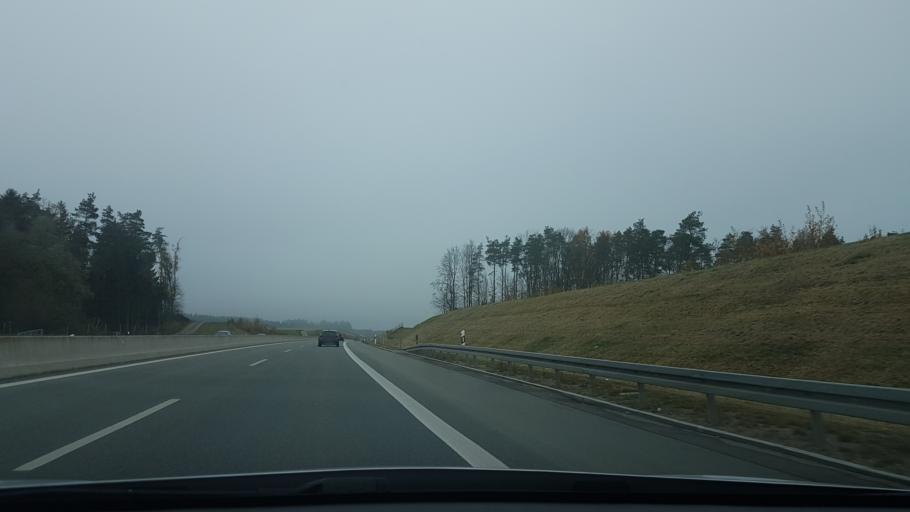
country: DE
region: Bavaria
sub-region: Lower Bavaria
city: Ergoldsbach
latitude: 48.6946
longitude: 12.1800
